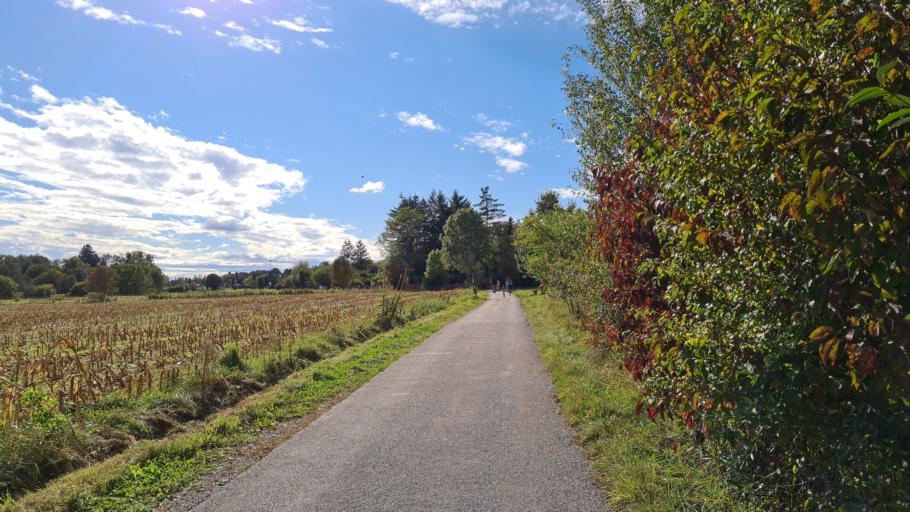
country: DE
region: Bavaria
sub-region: Upper Bavaria
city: Gauting
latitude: 48.0792
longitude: 11.3932
